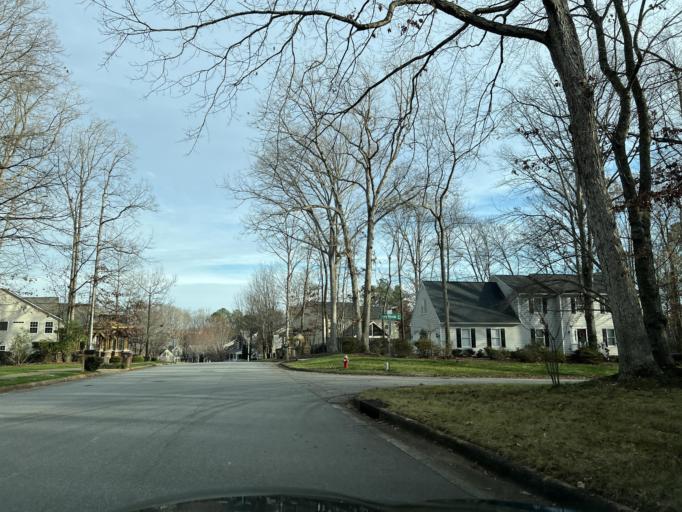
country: US
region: North Carolina
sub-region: Wake County
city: Cary
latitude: 35.8015
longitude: -78.7450
